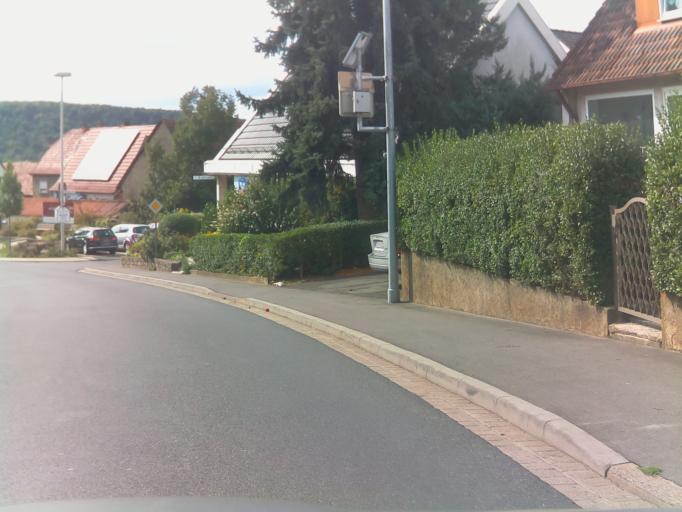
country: DE
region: Bavaria
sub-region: Regierungsbezirk Unterfranken
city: Zellingen
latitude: 49.9046
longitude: 9.8225
